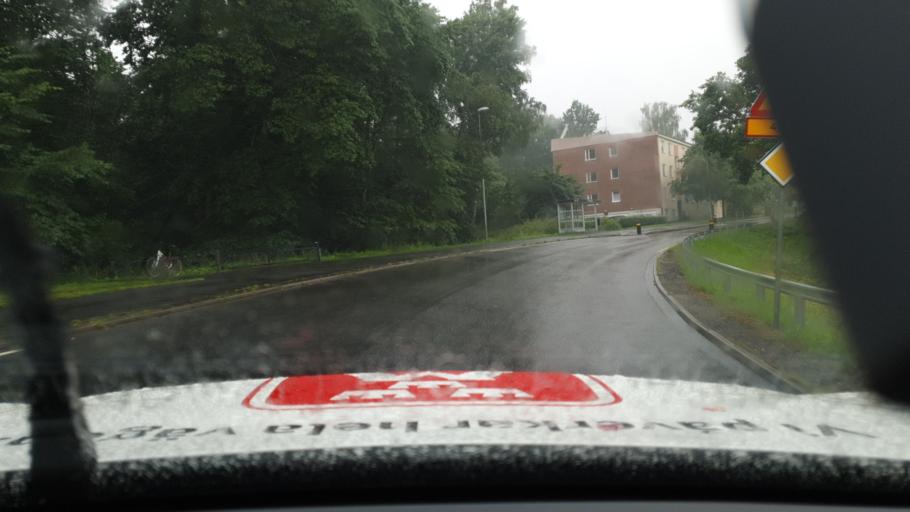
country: SE
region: Vaestra Goetaland
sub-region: Skovde Kommun
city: Skultorp
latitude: 58.3415
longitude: 13.8354
